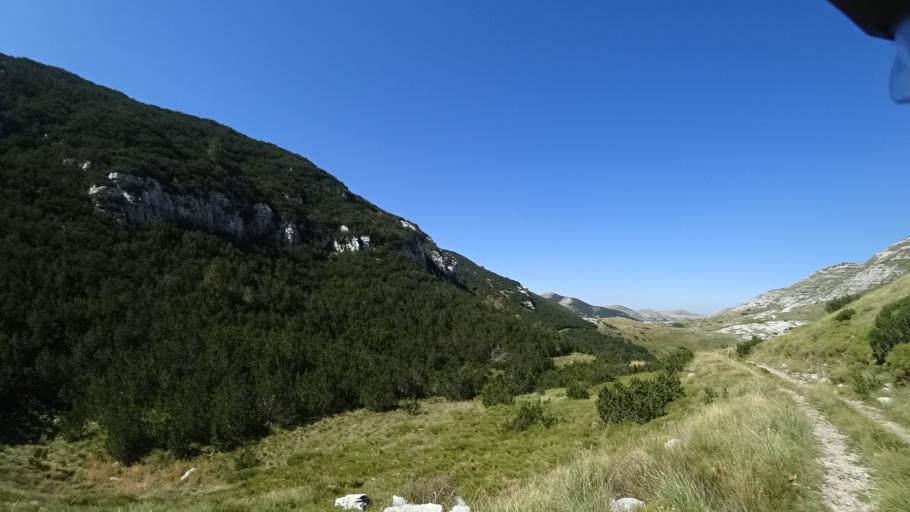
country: HR
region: Splitsko-Dalmatinska
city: Hrvace
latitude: 43.9351
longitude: 16.5981
